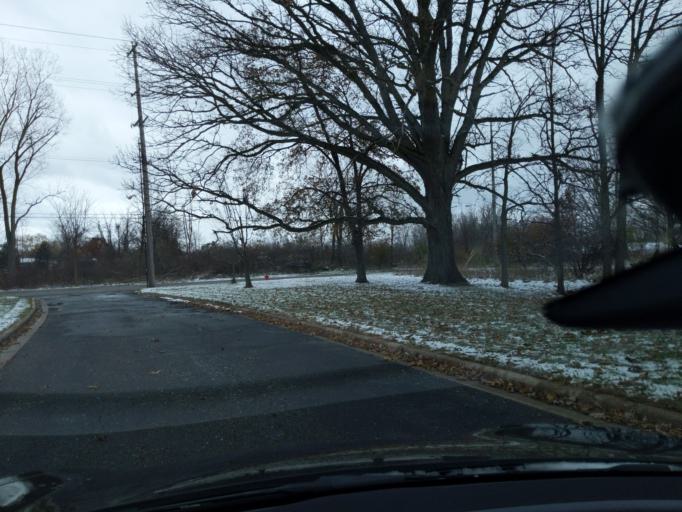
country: US
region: Michigan
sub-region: Ingham County
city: Lansing
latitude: 42.6781
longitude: -84.5917
